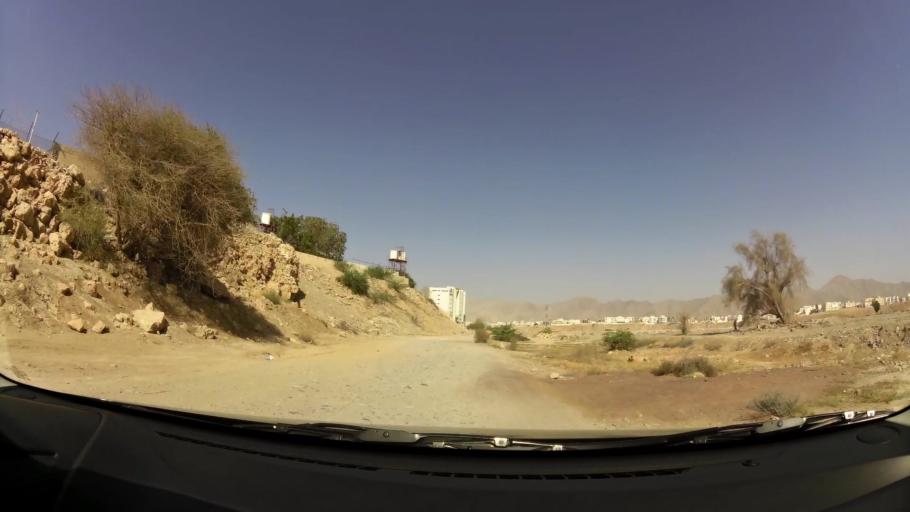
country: OM
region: Muhafazat Masqat
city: Bawshar
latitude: 23.5662
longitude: 58.3490
